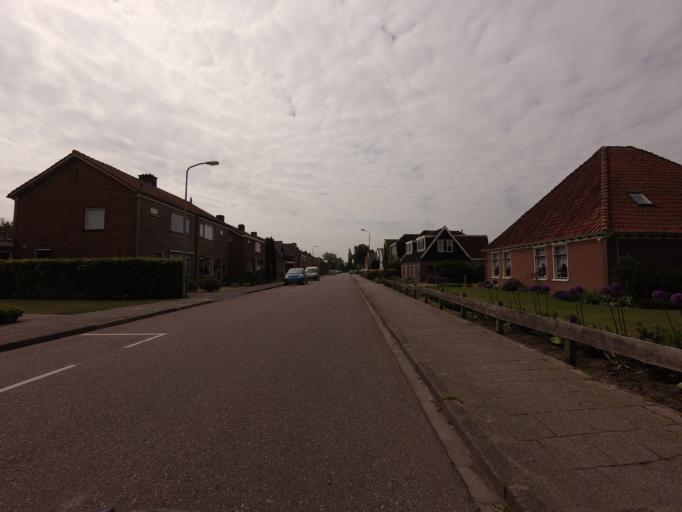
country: NL
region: North Holland
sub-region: Gemeente Hoorn
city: Hoorn
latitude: 52.6957
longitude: 5.0566
